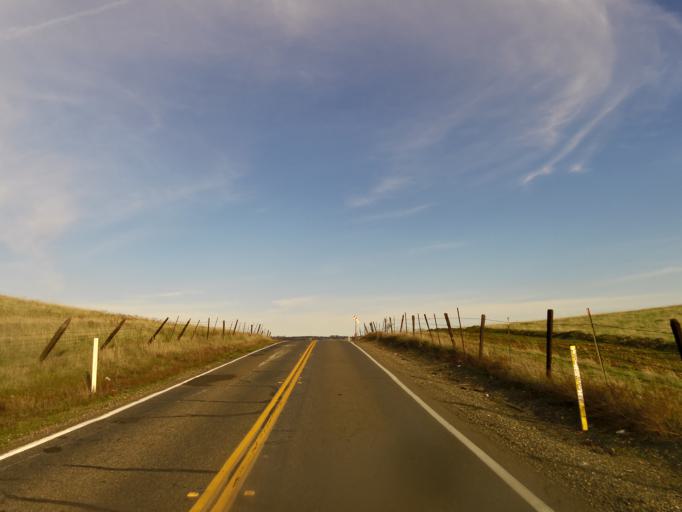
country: US
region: California
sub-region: El Dorado County
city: El Dorado Hills
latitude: 38.6281
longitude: -121.0848
